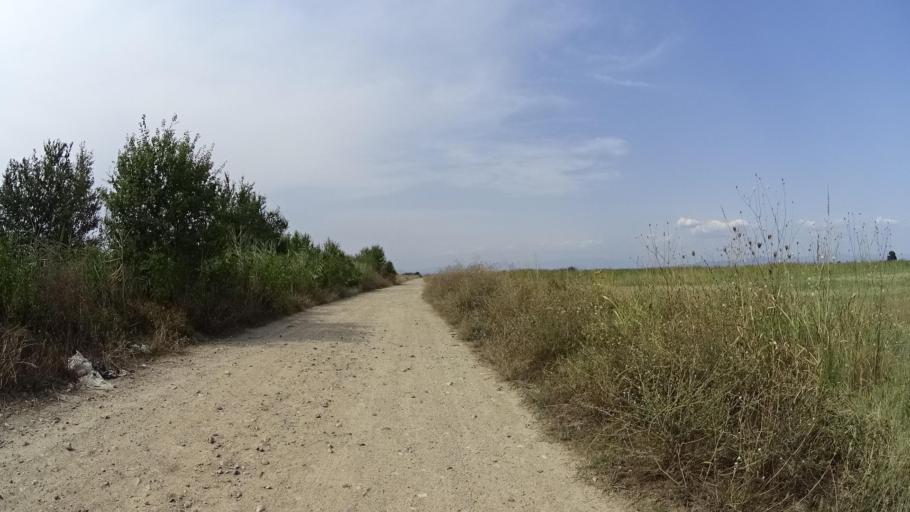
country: BG
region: Plovdiv
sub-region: Obshtina Kaloyanovo
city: Kaloyanovo
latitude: 42.2843
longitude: 24.7980
